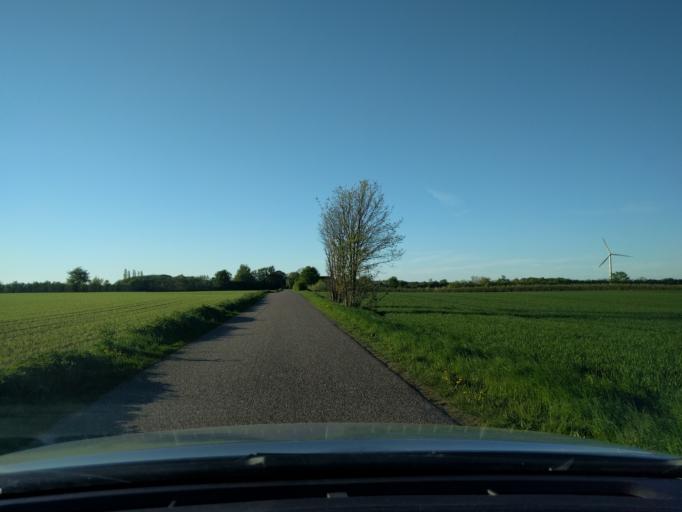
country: DK
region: South Denmark
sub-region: Nyborg Kommune
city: Ullerslev
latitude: 55.3928
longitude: 10.6496
